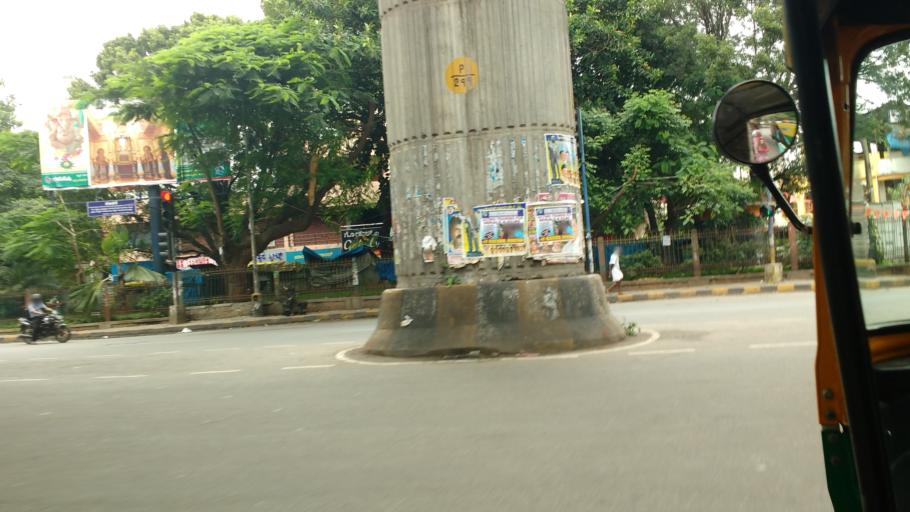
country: IN
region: Karnataka
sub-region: Bangalore Urban
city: Bangalore
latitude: 12.9730
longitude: 77.5385
